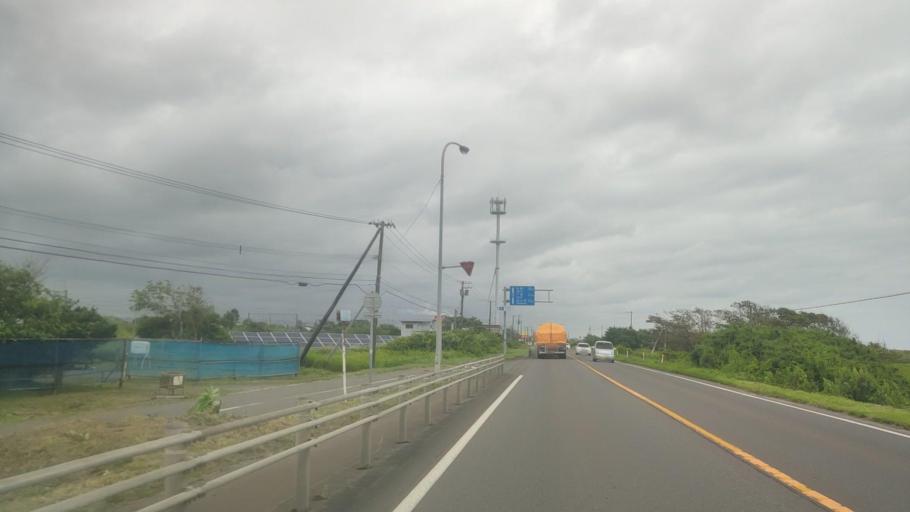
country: JP
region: Hokkaido
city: Shiraoi
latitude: 42.4931
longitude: 141.2624
